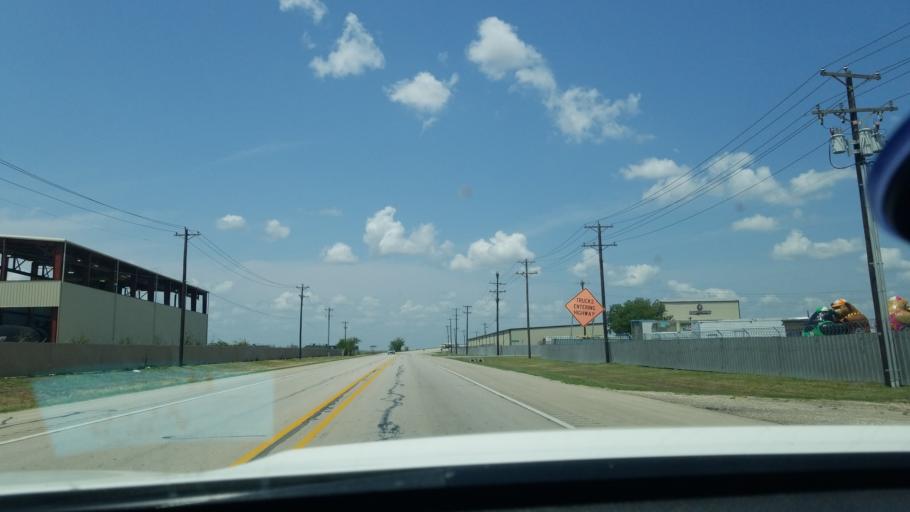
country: US
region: Texas
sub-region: Tarrant County
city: Eagle Mountain
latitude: 32.9382
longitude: -97.4193
